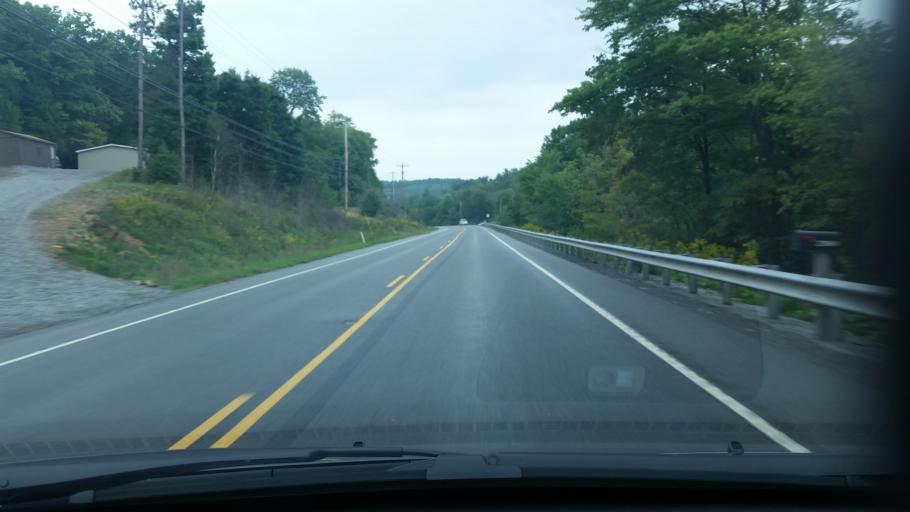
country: US
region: Pennsylvania
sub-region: Clearfield County
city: Shiloh
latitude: 41.0953
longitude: -78.2461
